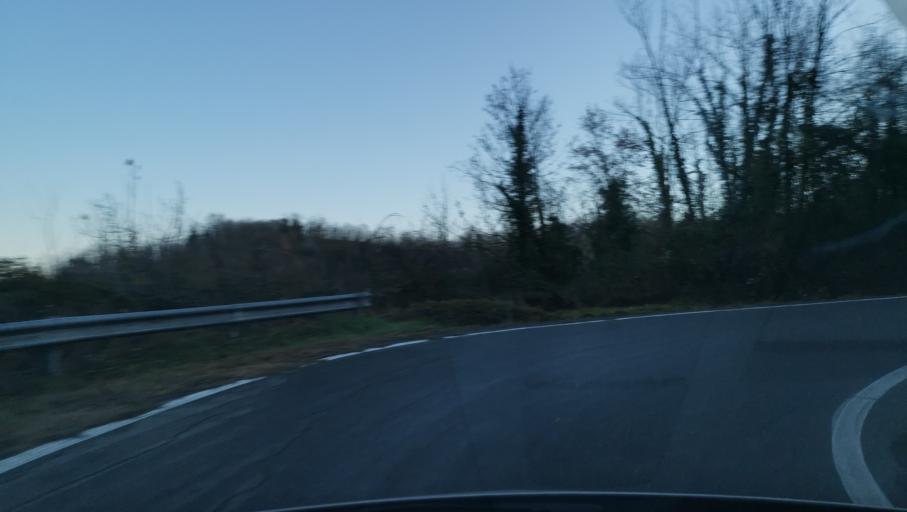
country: IT
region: Piedmont
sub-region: Provincia di Torino
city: Cinzano
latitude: 45.1068
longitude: 7.9271
